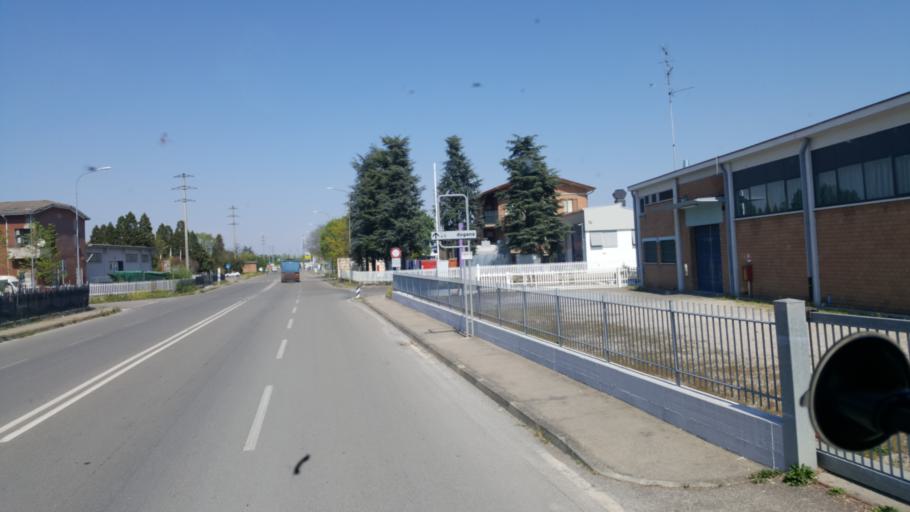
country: IT
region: Emilia-Romagna
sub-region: Provincia di Reggio Emilia
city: Reggio nell'Emilia
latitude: 44.7304
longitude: 10.6495
